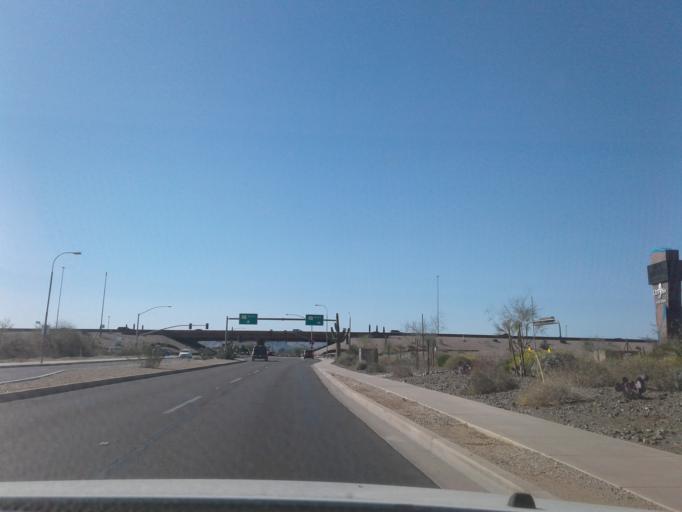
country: US
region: Arizona
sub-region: Maricopa County
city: Scottsdale
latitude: 33.5536
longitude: -111.8774
